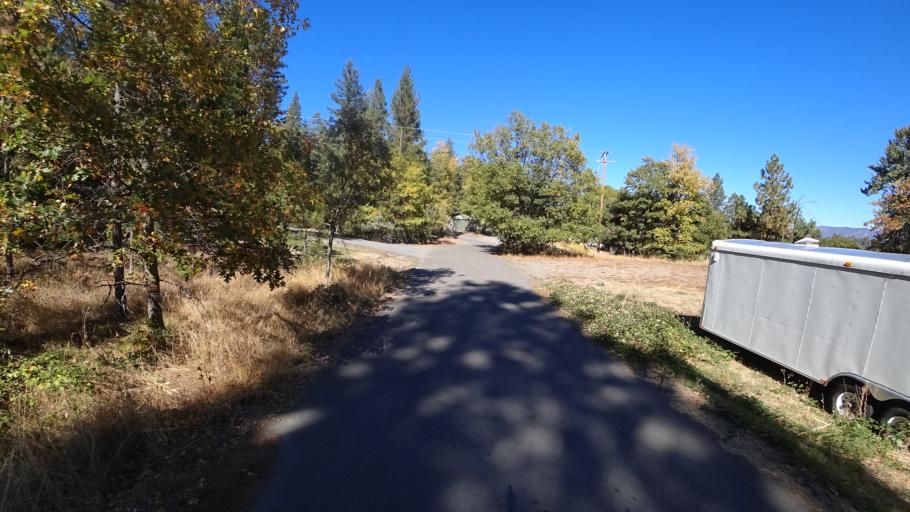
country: US
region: California
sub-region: Siskiyou County
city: Yreka
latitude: 41.4568
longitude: -122.9030
